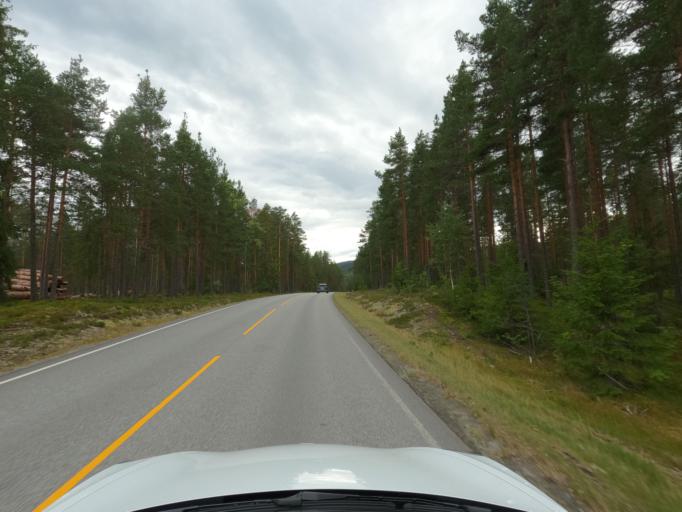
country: NO
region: Telemark
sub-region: Hjartdal
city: Sauland
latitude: 59.7167
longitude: 9.0177
